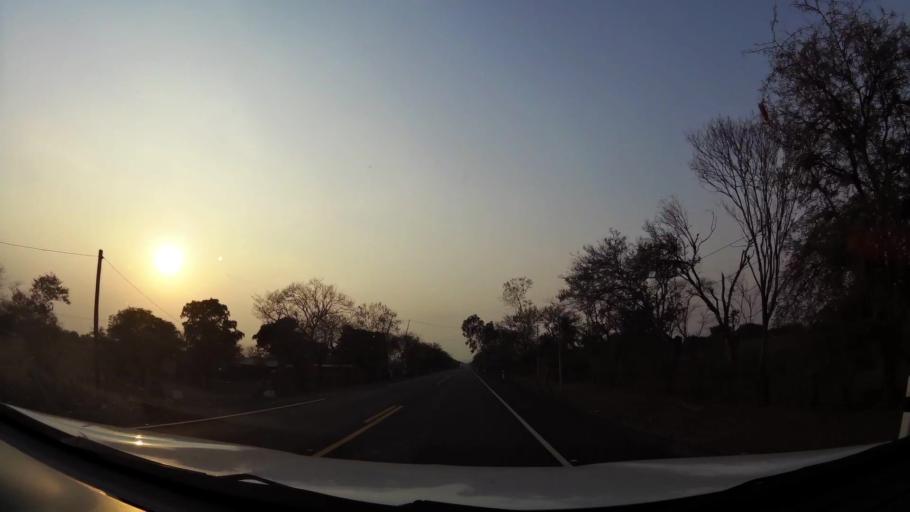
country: NI
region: Leon
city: Nagarote
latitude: 12.3009
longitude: -86.5963
